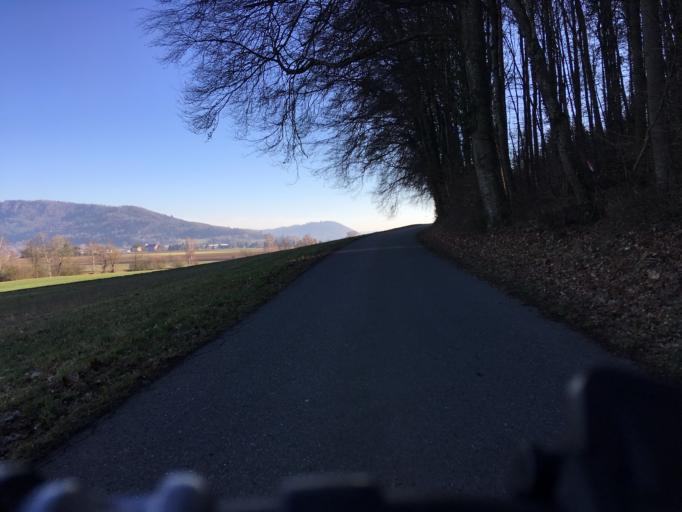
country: CH
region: Schaffhausen
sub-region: Bezirk Stein
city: Ramsen
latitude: 47.7203
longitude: 8.8081
